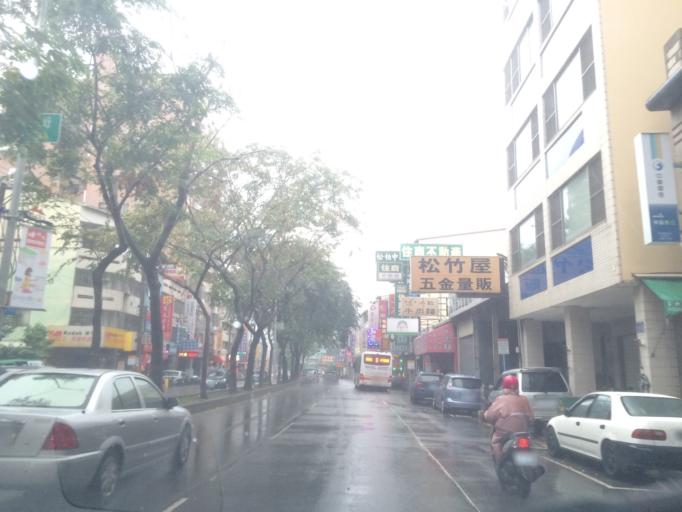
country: TW
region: Taiwan
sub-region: Taichung City
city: Taichung
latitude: 24.1833
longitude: 120.6946
